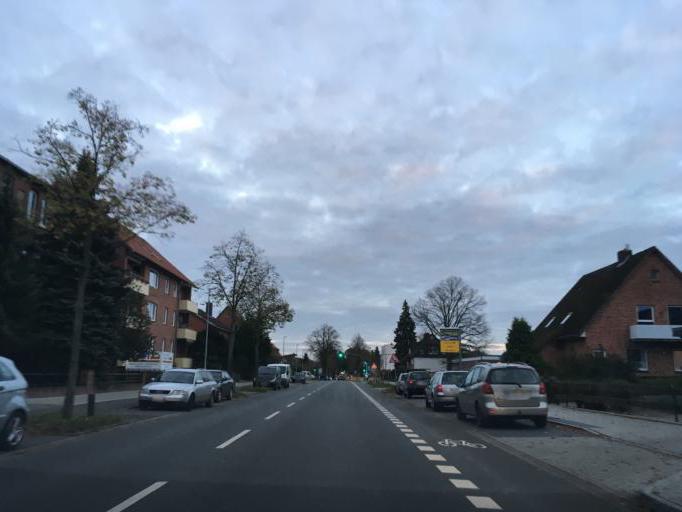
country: DE
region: Lower Saxony
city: Lueneburg
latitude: 53.2455
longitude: 10.4412
